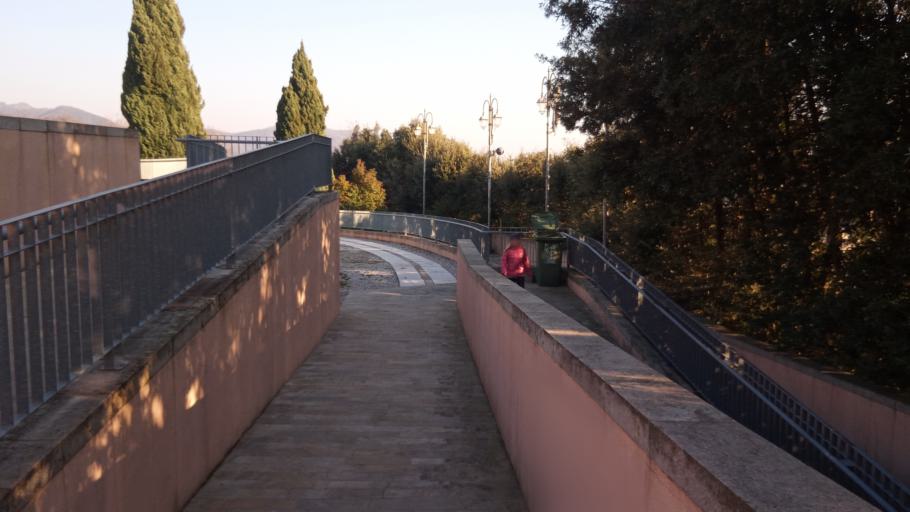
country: IT
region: Veneto
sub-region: Provincia di Padova
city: Galzignano
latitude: 45.3127
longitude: 11.7319
